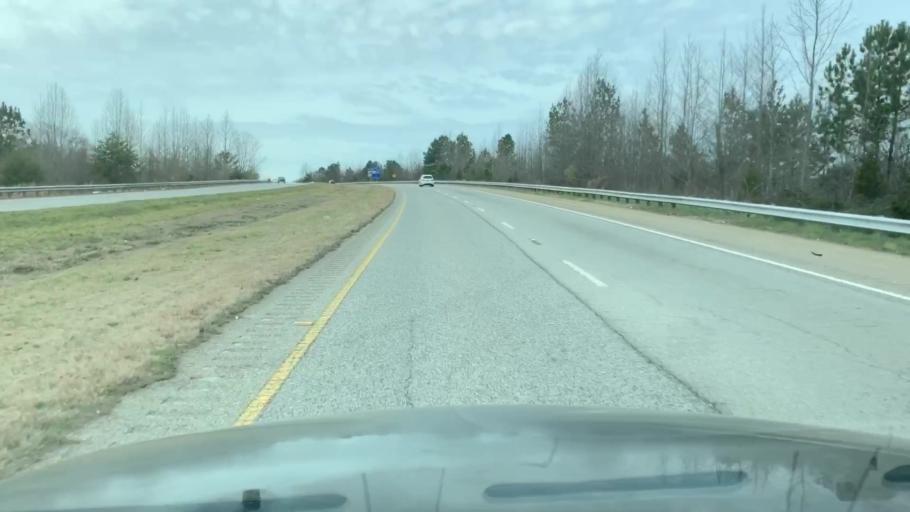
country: US
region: South Carolina
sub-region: Greenville County
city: Golden Grove
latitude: 34.7228
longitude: -82.3746
